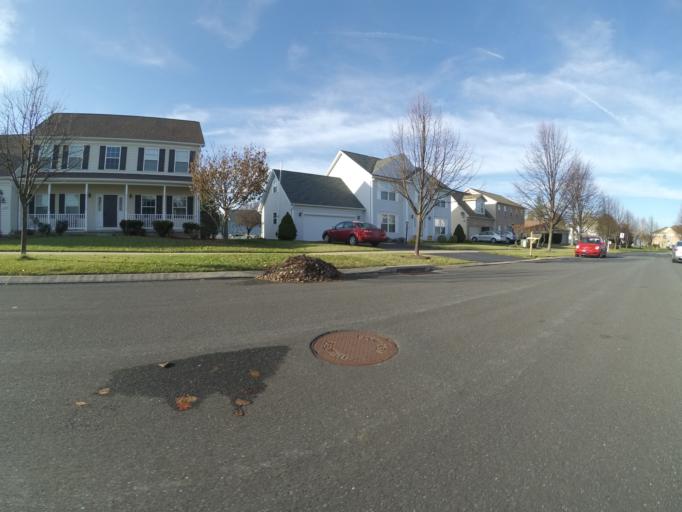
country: US
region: Pennsylvania
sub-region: Centre County
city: Pine Grove Mills
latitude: 40.7660
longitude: -77.8924
